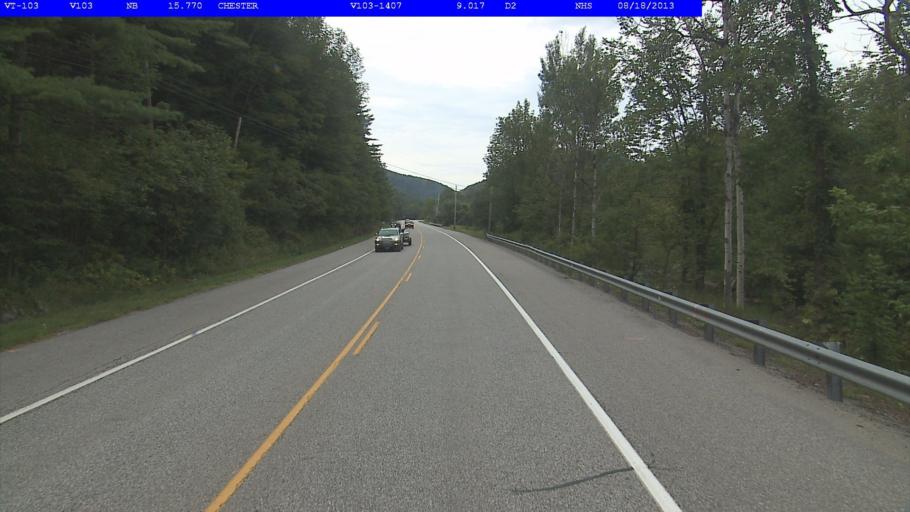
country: US
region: Vermont
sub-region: Windsor County
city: Chester
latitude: 43.3403
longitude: -72.6191
